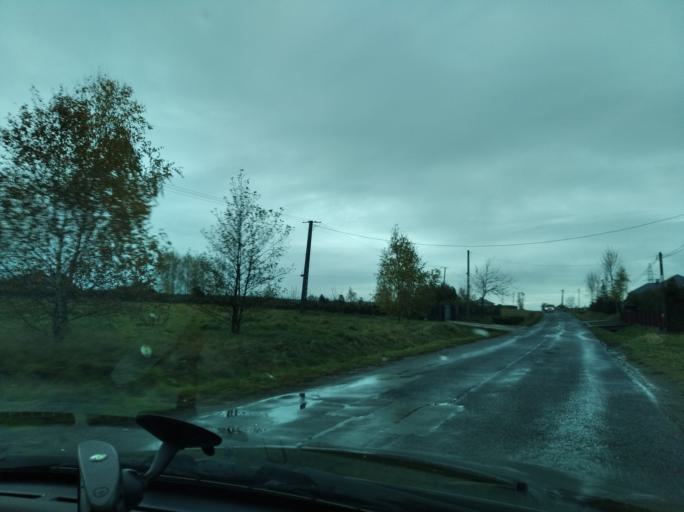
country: PL
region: Subcarpathian Voivodeship
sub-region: Powiat rzeszowski
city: Tyczyn
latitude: 49.9283
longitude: 22.0289
